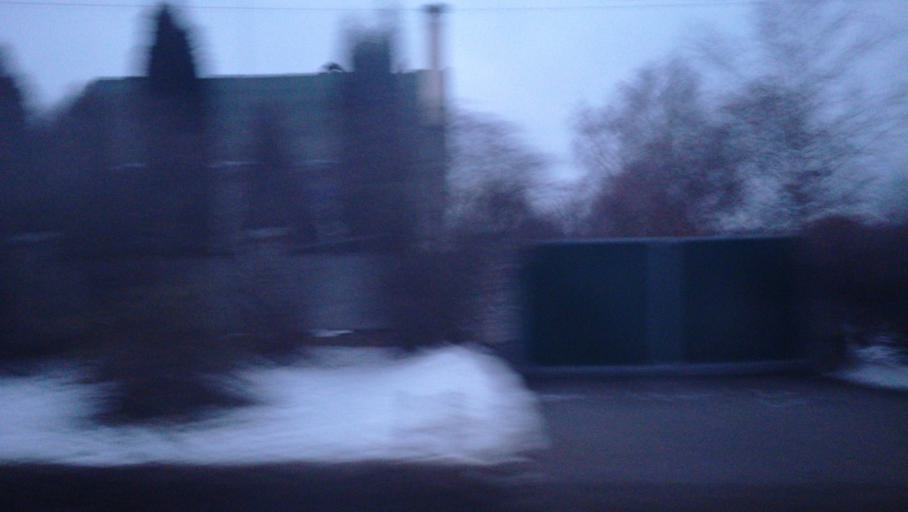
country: RU
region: Tula
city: Barsuki
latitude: 54.2054
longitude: 37.5349
